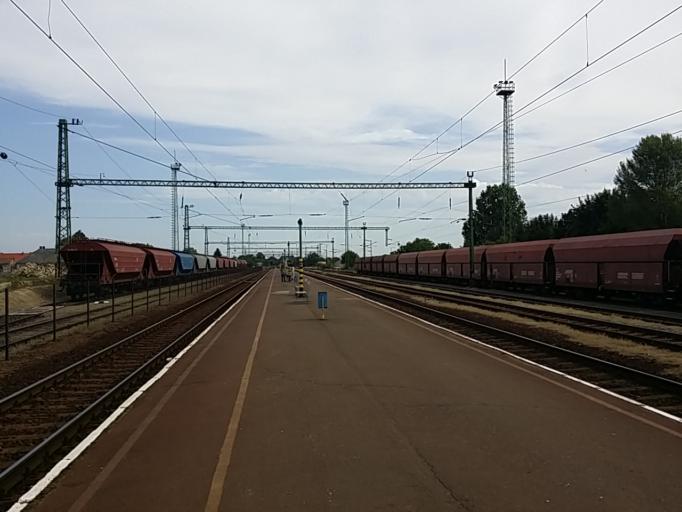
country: HU
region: Baranya
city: Szentlorinc
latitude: 46.0330
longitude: 17.9914
